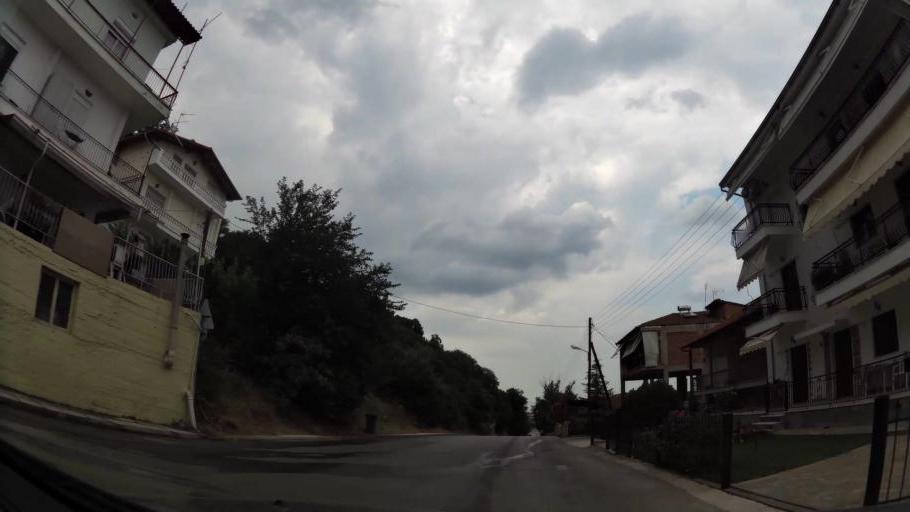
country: GR
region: Central Macedonia
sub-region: Nomos Imathias
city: Veroia
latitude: 40.5255
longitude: 22.2085
